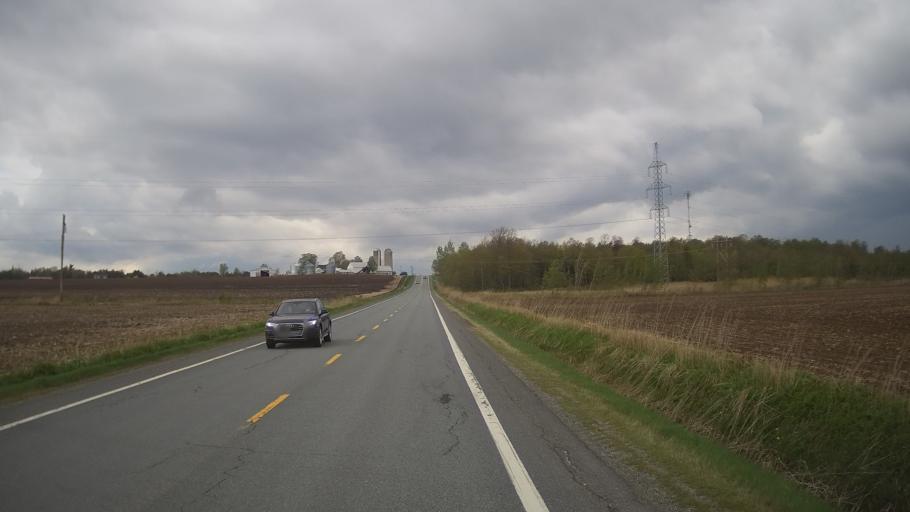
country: CA
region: Quebec
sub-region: Monteregie
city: Farnham
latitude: 45.2640
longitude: -72.9340
